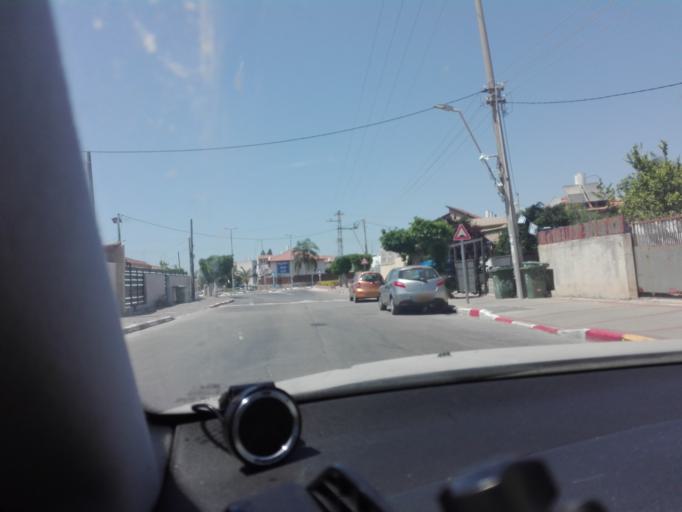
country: IL
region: Central District
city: Bene 'Ayish
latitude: 31.7342
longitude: 34.7475
